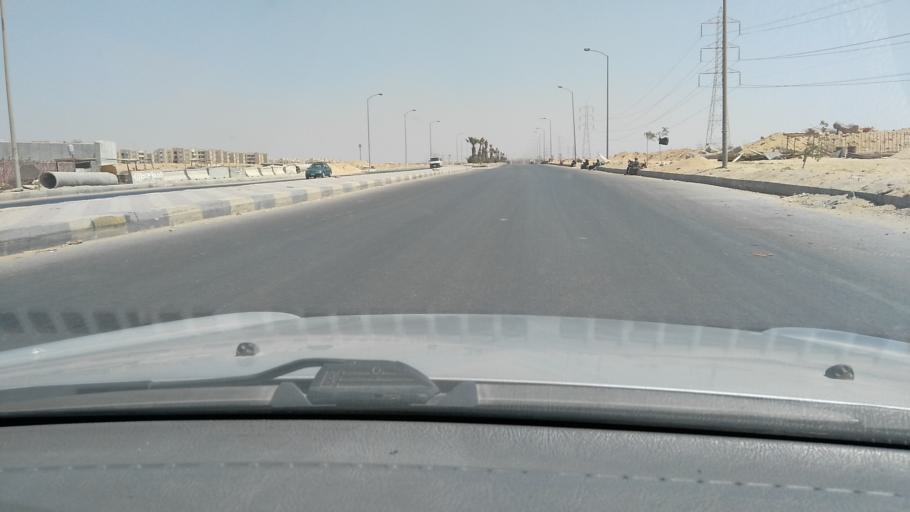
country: EG
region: Al Jizah
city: Madinat Sittah Uktubar
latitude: 29.9332
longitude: 30.9444
